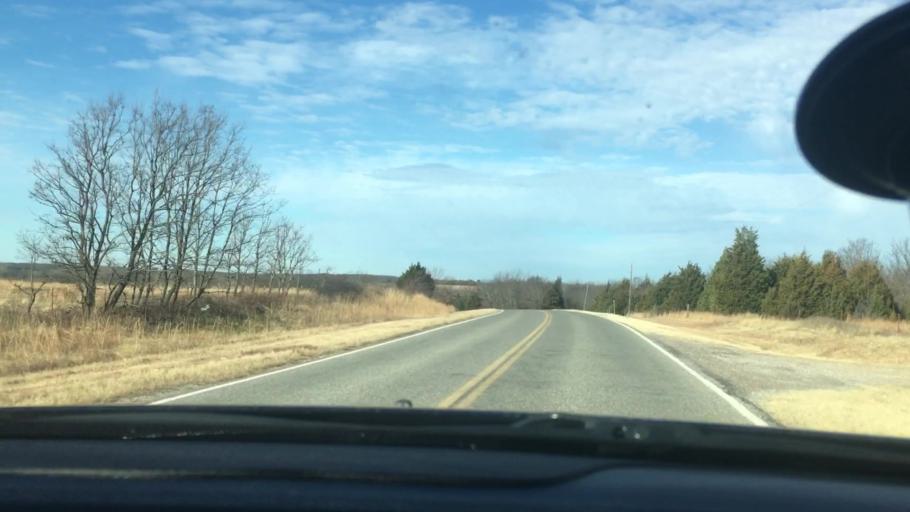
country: US
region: Oklahoma
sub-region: Seminole County
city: Konawa
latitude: 34.9847
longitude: -96.7969
